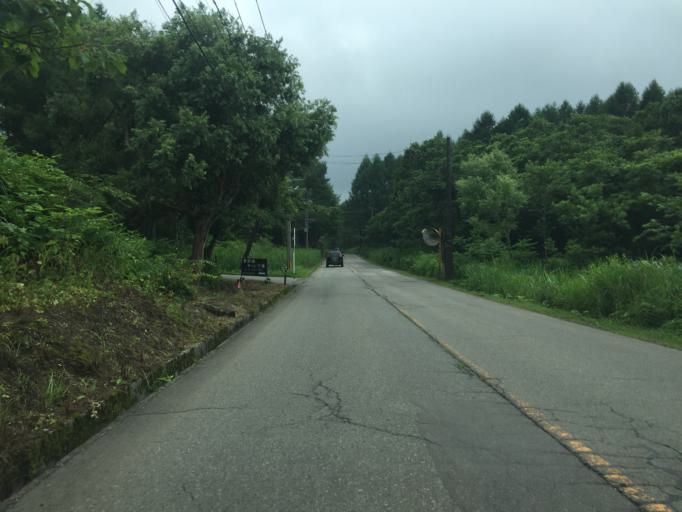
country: JP
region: Fukushima
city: Inawashiro
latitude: 37.6822
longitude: 140.0685
